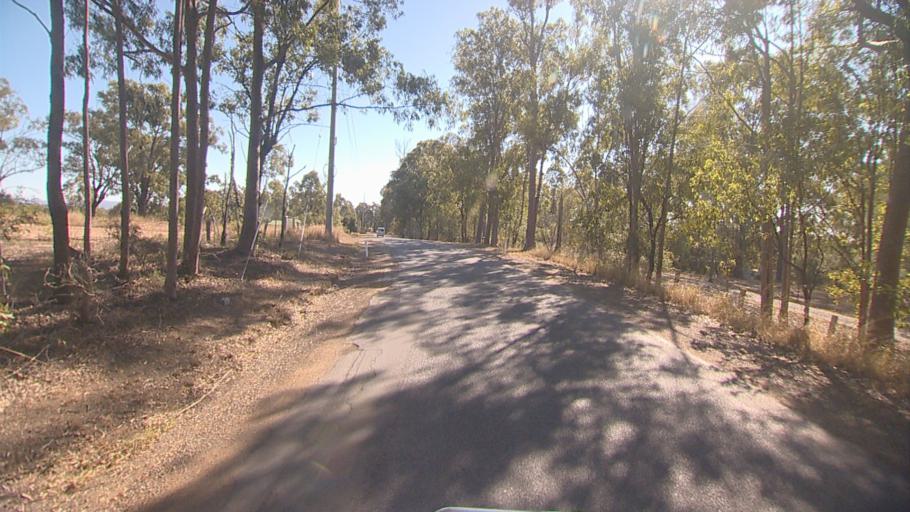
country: AU
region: Queensland
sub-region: Logan
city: Cedar Vale
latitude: -27.8924
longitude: 153.0181
